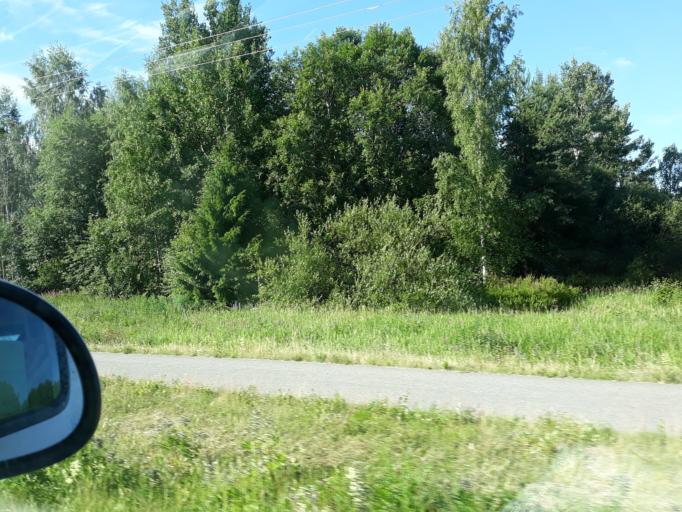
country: FI
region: Uusimaa
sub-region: Helsinki
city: Jaervenpaeae
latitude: 60.5454
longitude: 24.9851
